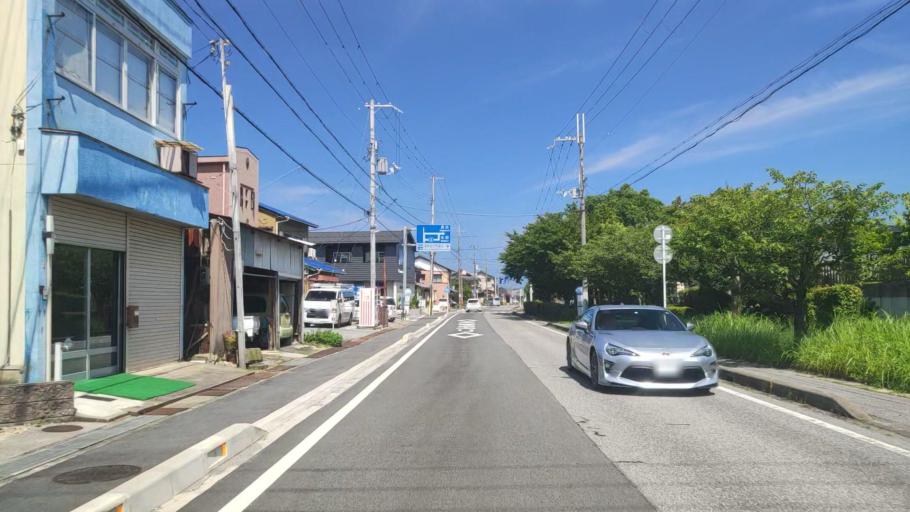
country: JP
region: Shiga Prefecture
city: Hikone
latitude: 35.2752
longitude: 136.2435
